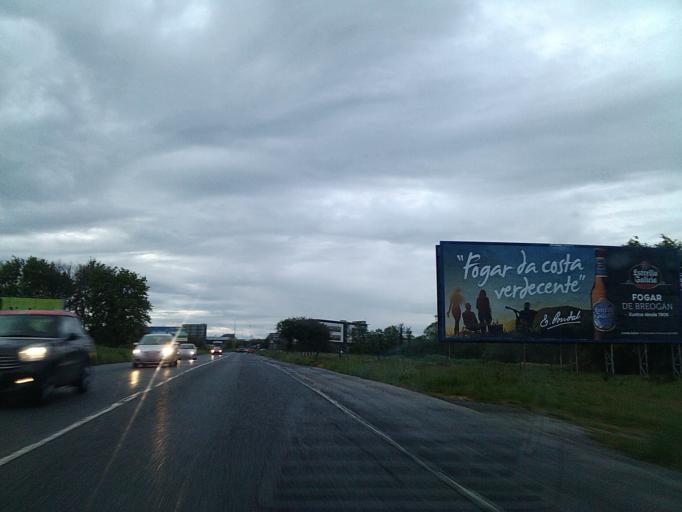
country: ES
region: Galicia
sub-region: Provincia de Lugo
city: Lugo
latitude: 43.0406
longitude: -7.5680
